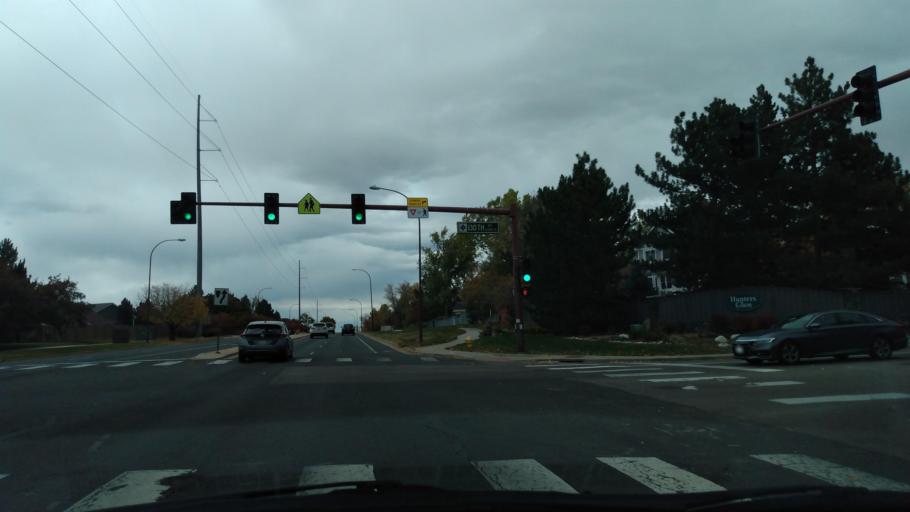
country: US
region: Colorado
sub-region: Adams County
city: Northglenn
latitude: 39.9318
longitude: -104.9779
